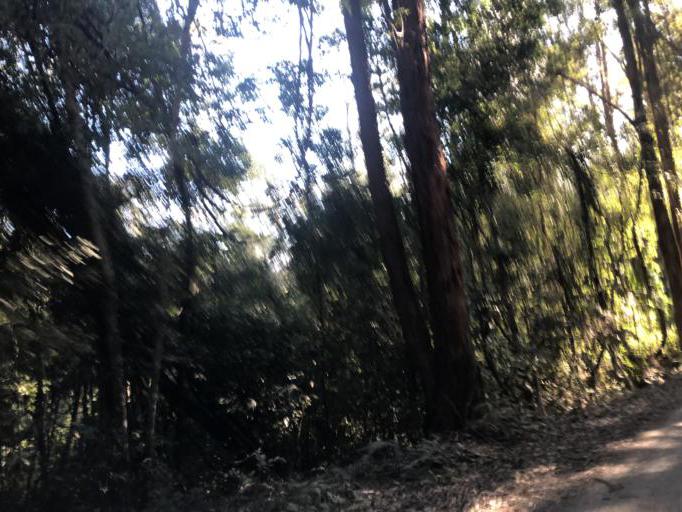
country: AU
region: New South Wales
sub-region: Bellingen
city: Bellingen
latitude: -30.4370
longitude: 152.8324
